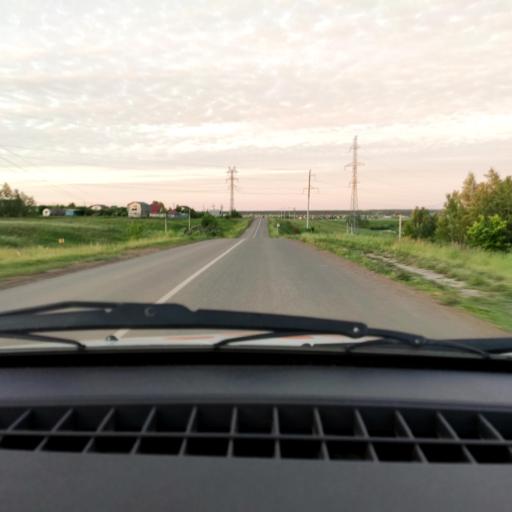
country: RU
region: Bashkortostan
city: Avdon
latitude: 54.5726
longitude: 55.7554
